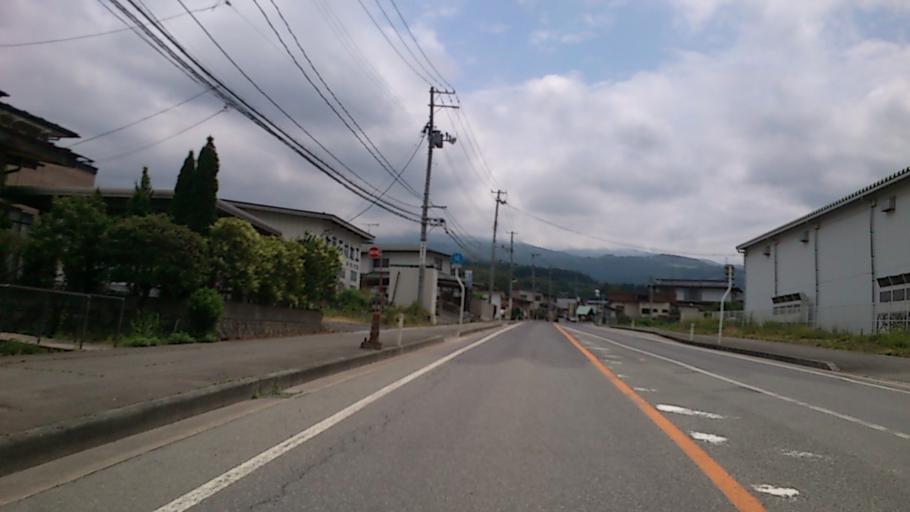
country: JP
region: Yamagata
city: Kaminoyama
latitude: 38.1623
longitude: 140.3083
